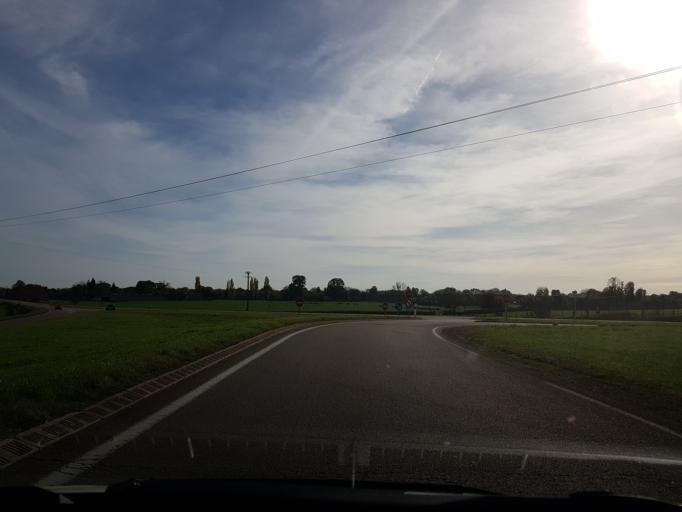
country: FR
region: Bourgogne
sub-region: Departement de l'Yonne
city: Avallon
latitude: 47.4867
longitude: 3.9904
